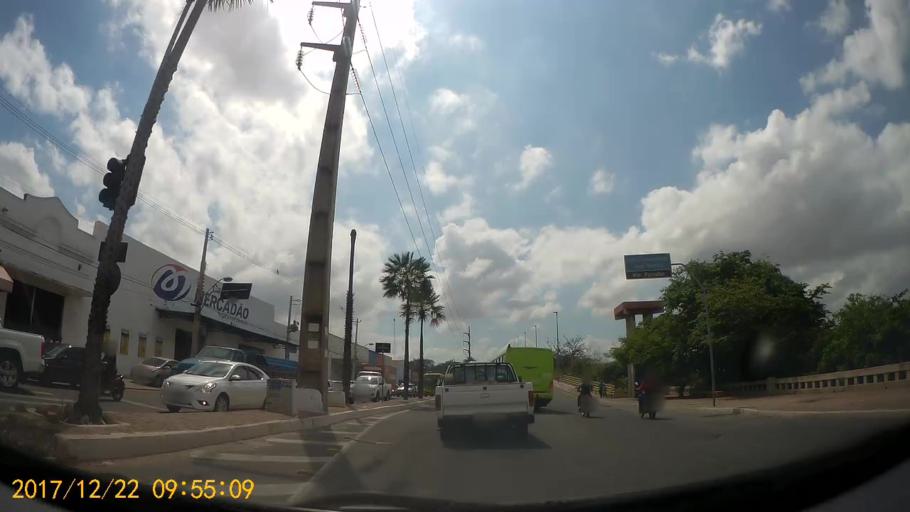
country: BR
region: Piaui
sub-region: Teresina
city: Teresina
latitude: -5.0963
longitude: -42.8166
